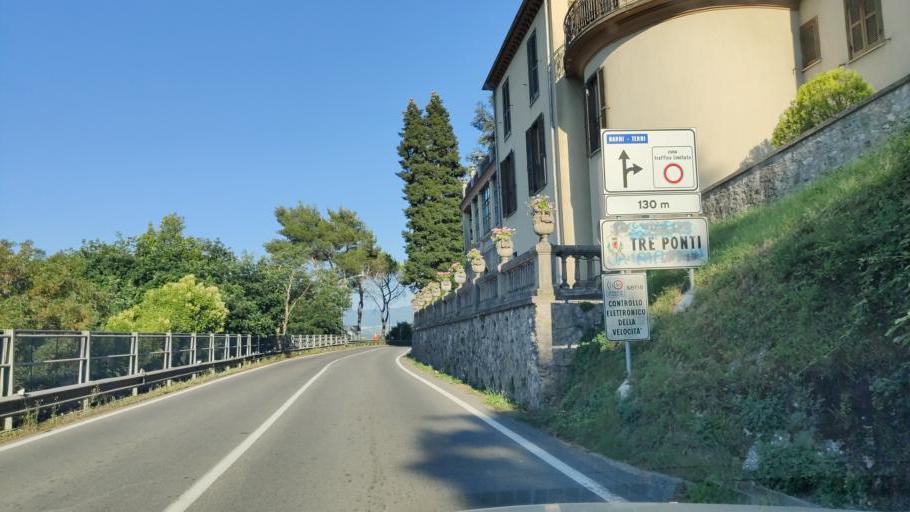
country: IT
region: Umbria
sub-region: Provincia di Terni
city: Narni Scalo
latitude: 42.5246
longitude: 12.5150
